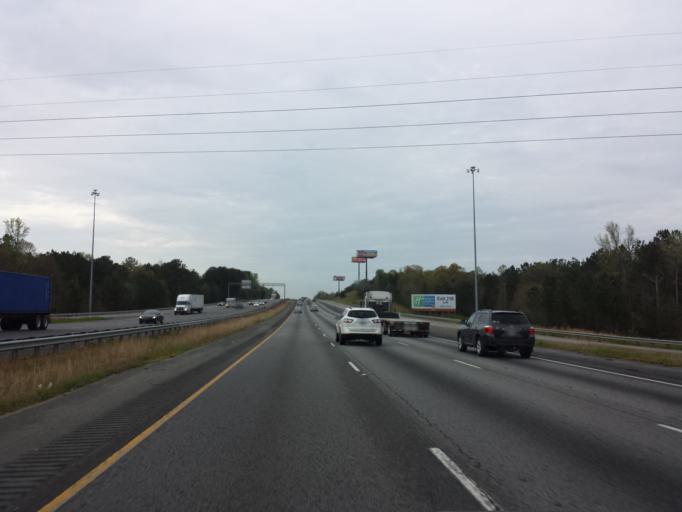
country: US
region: Georgia
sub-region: Henry County
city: Locust Grove
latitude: 33.2649
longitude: -84.0975
